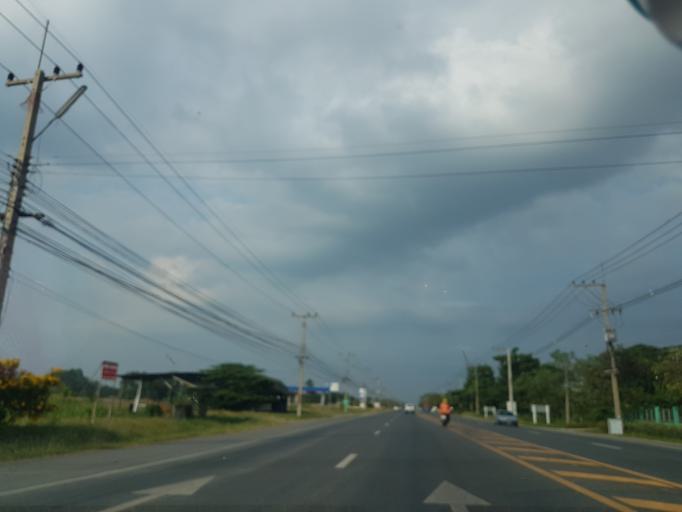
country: TH
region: Sara Buri
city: Phra Phutthabat
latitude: 14.6818
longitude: 100.7748
